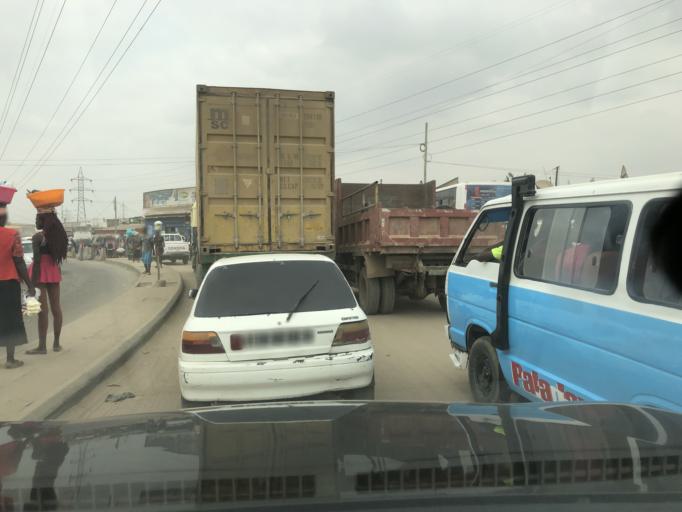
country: AO
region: Luanda
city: Luanda
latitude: -8.8164
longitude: 13.2780
